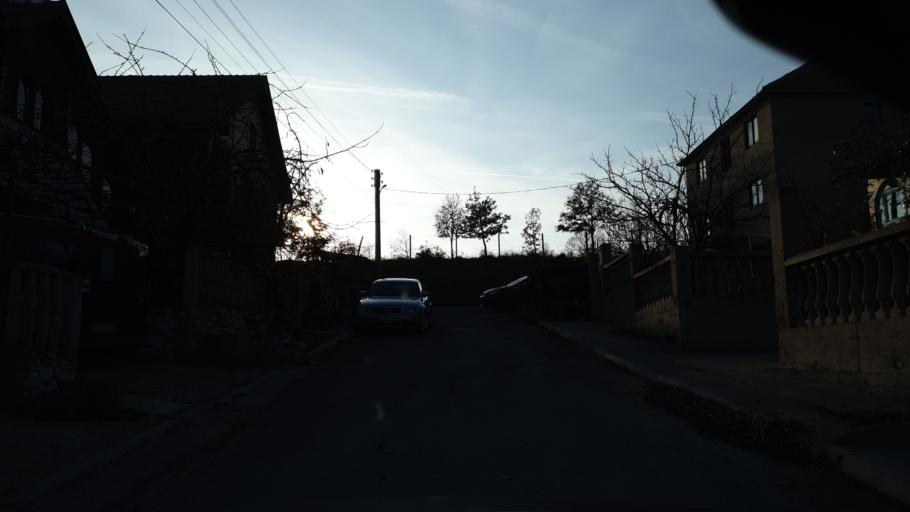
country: RS
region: Central Serbia
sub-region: Borski Okrug
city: Bor
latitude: 44.0533
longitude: 22.0870
